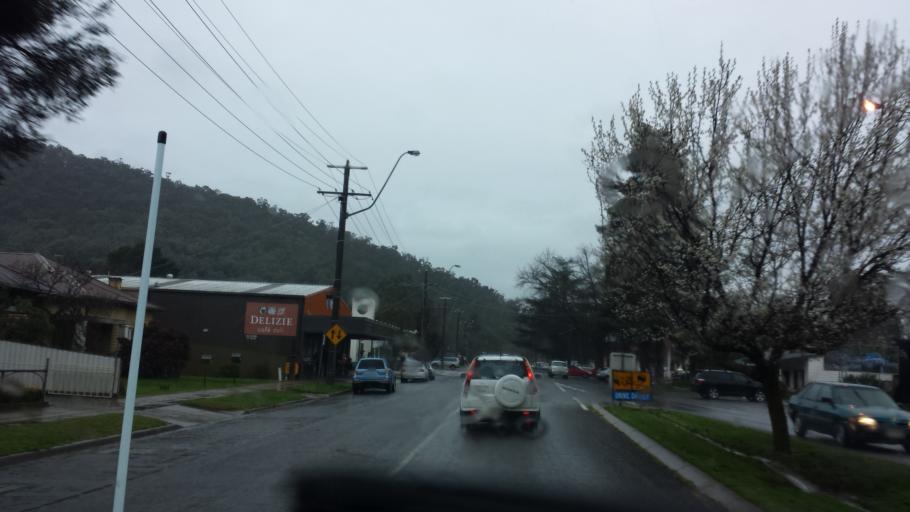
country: AU
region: Victoria
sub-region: Wangaratta
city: Wangaratta
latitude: -36.5635
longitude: 146.7277
